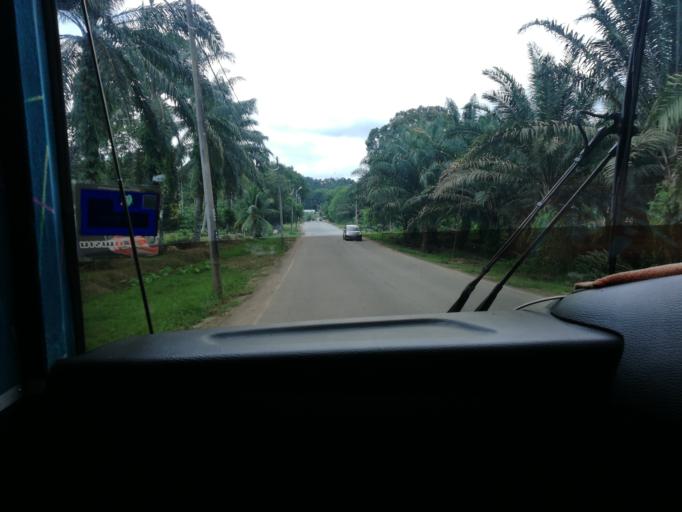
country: MY
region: Perak
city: Parit Buntar
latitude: 5.1617
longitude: 100.5943
